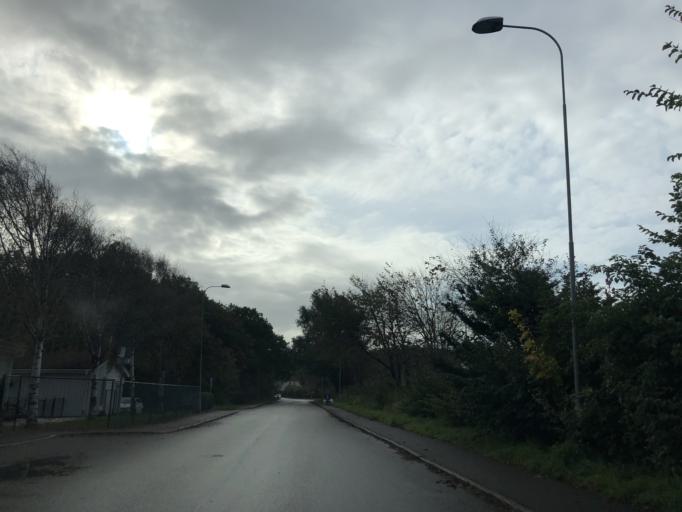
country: SE
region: Vaestra Goetaland
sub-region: Goteborg
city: Majorna
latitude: 57.6651
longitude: 11.8619
